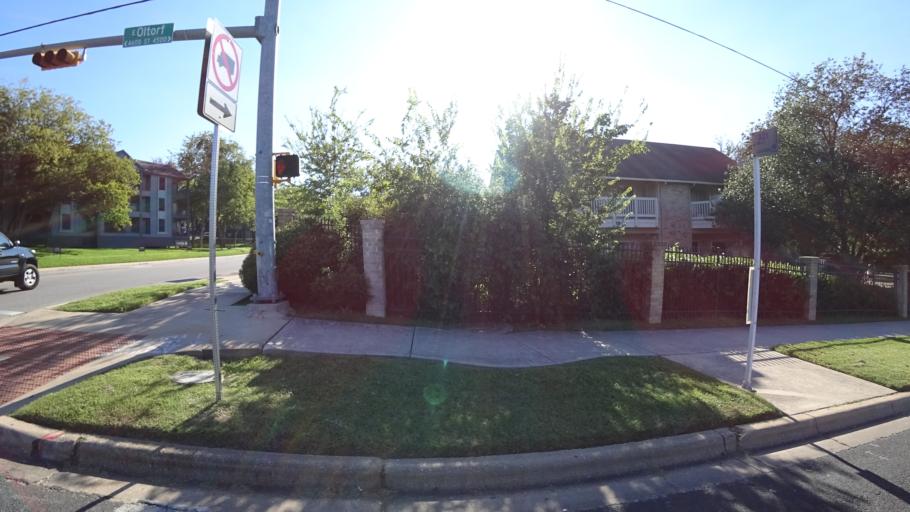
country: US
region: Texas
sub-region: Travis County
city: Austin
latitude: 30.2257
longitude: -97.7245
